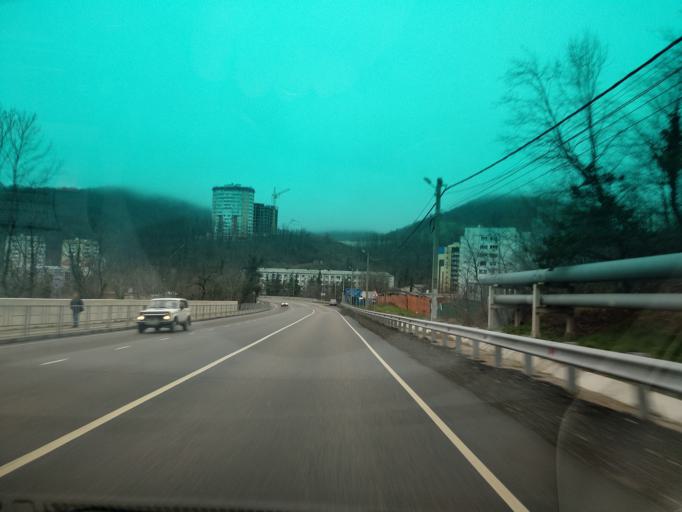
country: RU
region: Krasnodarskiy
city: Tuapse
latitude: 44.1148
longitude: 39.0692
